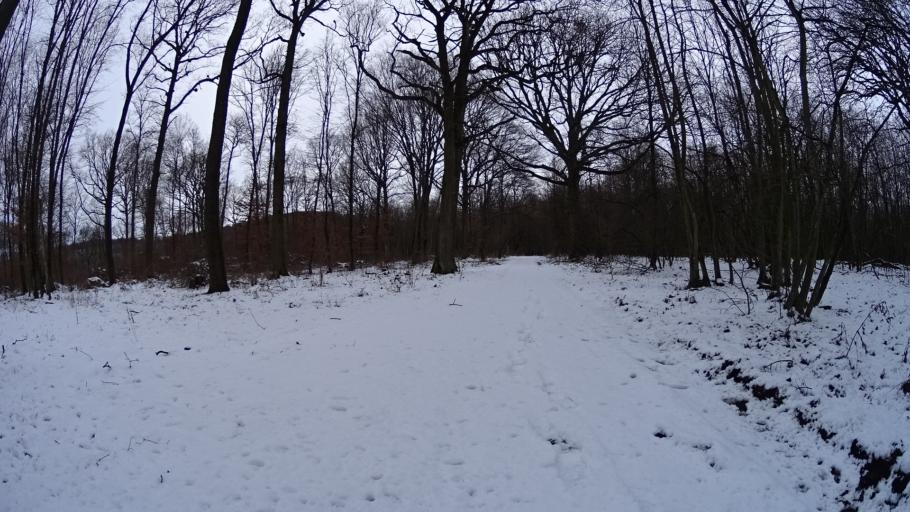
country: AT
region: Lower Austria
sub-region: Politischer Bezirk Korneuburg
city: Niederhollabrunn
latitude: 48.4181
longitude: 16.2976
